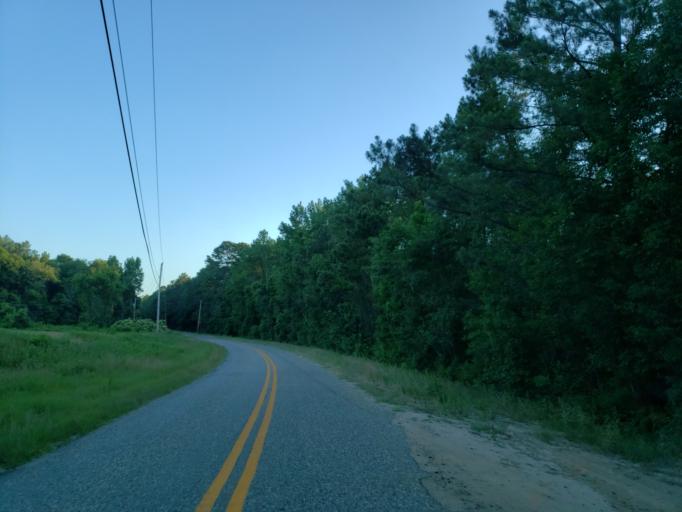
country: US
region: Georgia
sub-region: Crisp County
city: Cordele
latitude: 32.0198
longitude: -83.7537
